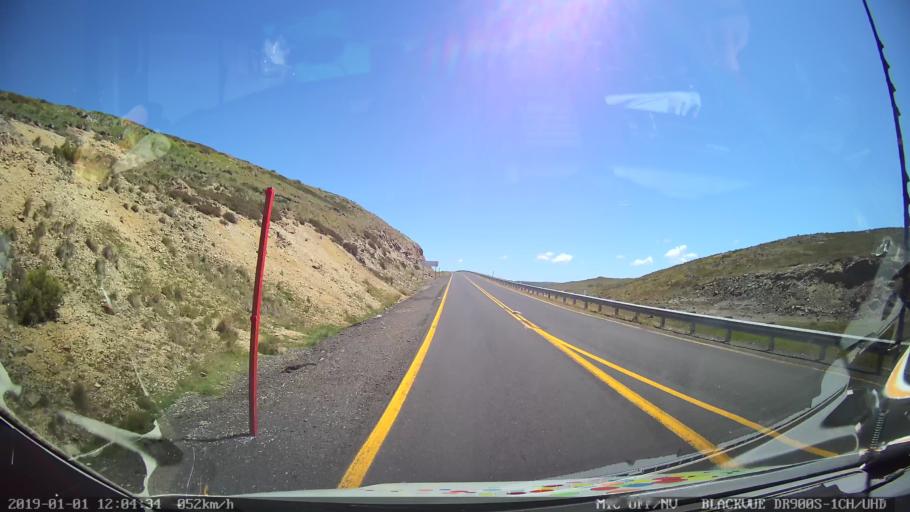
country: AU
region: New South Wales
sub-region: Snowy River
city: Jindabyne
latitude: -35.8659
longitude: 148.4969
